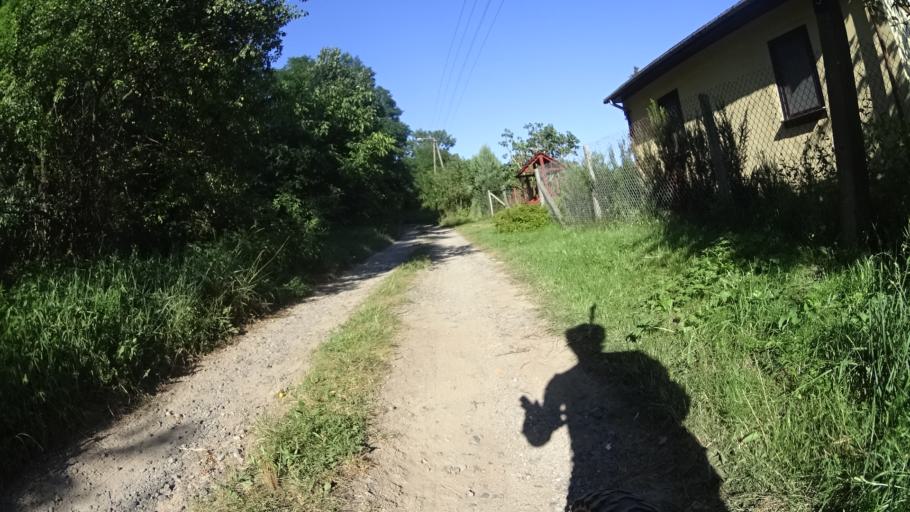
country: PL
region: Masovian Voivodeship
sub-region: Powiat bialobrzeski
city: Wysmierzyce
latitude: 51.6616
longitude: 20.8493
